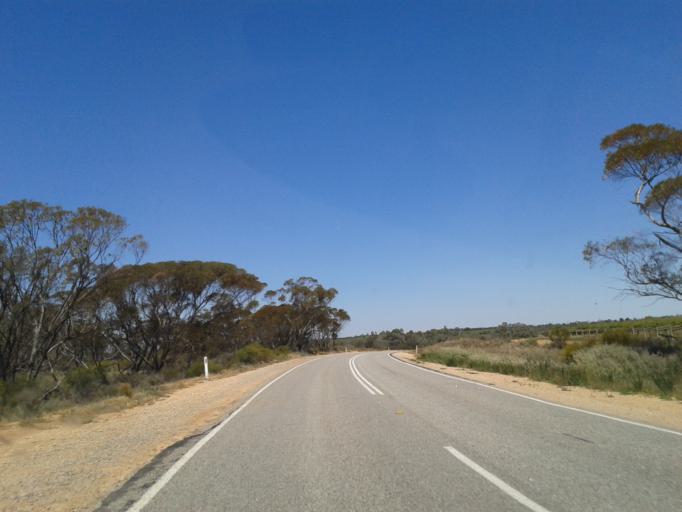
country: AU
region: Victoria
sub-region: Mildura Shire
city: Ouyen
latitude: -34.6554
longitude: 142.8337
